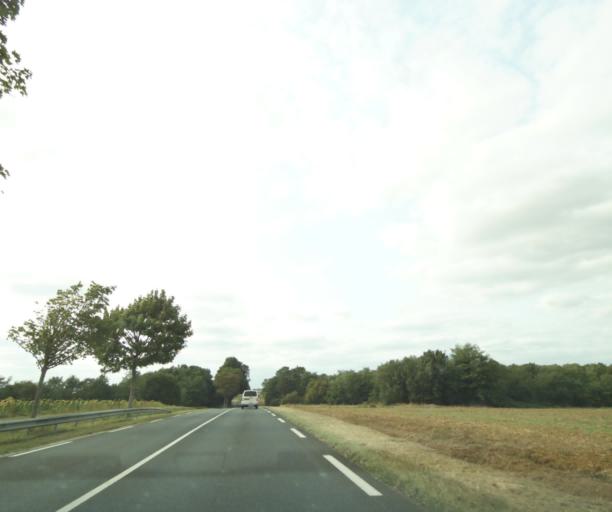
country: FR
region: Centre
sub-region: Departement d'Indre-et-Loire
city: Reignac-sur-Indre
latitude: 47.2300
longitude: 0.8763
